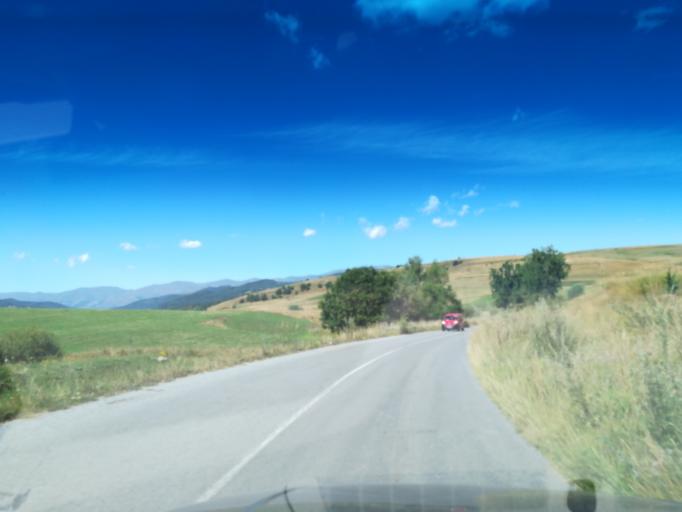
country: BG
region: Sofiya
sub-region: Obshtina Koprivshtitsa
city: Koprivshtitsa
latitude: 42.6009
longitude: 24.3795
